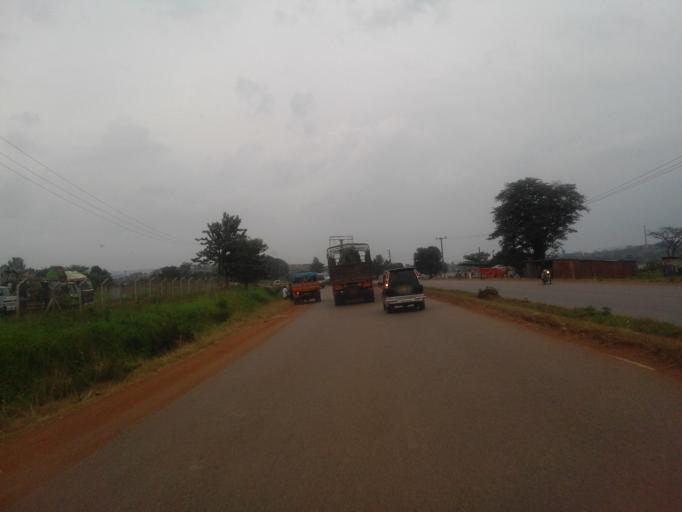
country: UG
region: Eastern Region
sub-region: Jinja District
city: Jinja
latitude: 0.4419
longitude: 33.2147
